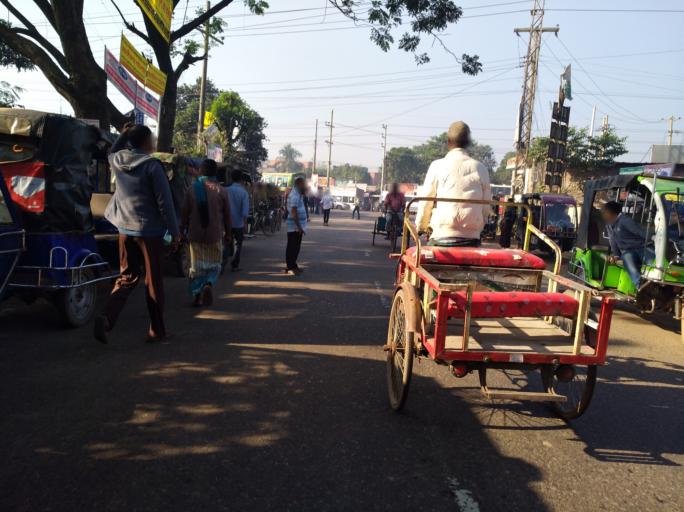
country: BD
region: Dhaka
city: Tungi
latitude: 23.8966
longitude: 90.2712
